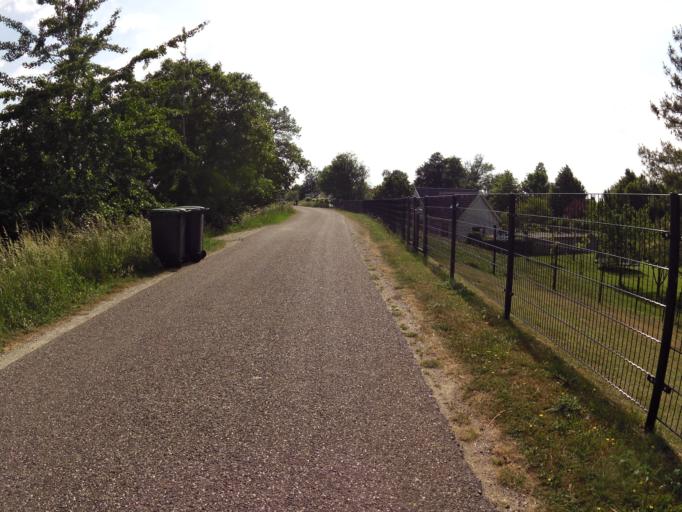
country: NL
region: Gelderland
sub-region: Gemeente Neerijnen
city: Neerijnen
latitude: 51.7956
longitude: 5.3275
